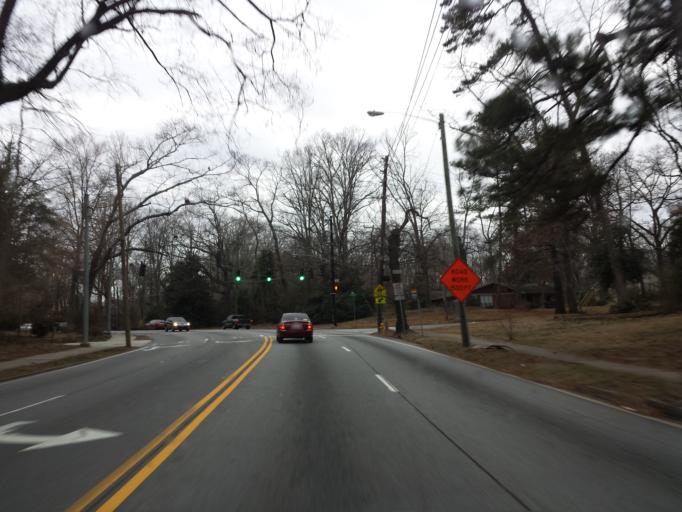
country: US
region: Georgia
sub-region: DeKalb County
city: North Decatur
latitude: 33.7742
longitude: -84.3156
